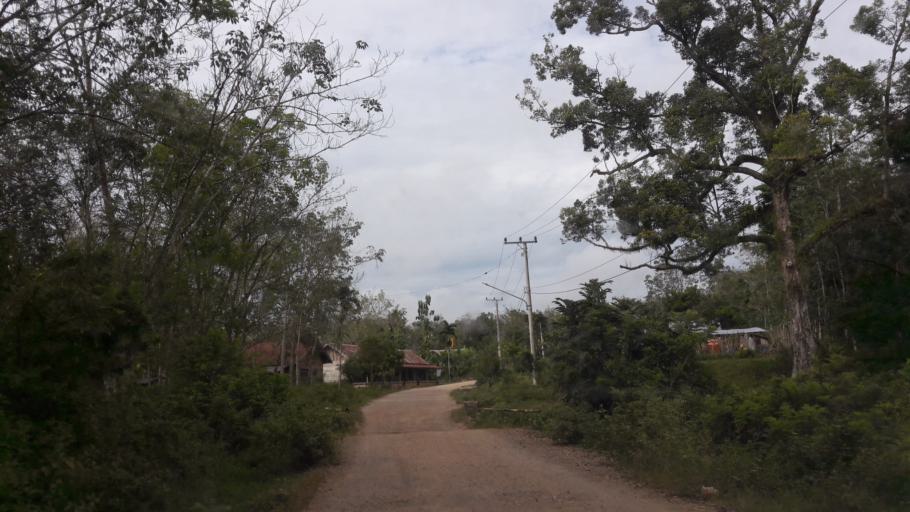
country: ID
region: South Sumatra
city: Gunungmegang Dalam
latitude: -3.2926
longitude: 103.6776
